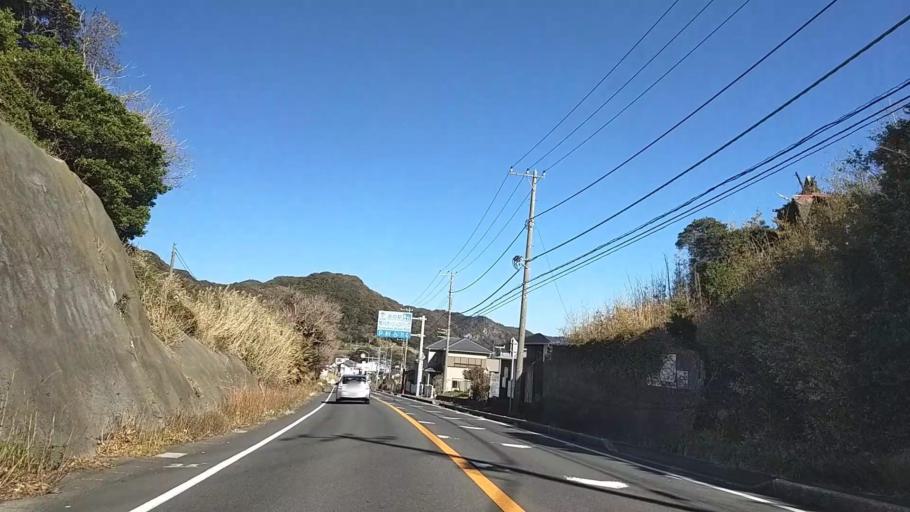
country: JP
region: Chiba
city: Kawaguchi
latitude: 35.0603
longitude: 140.0727
